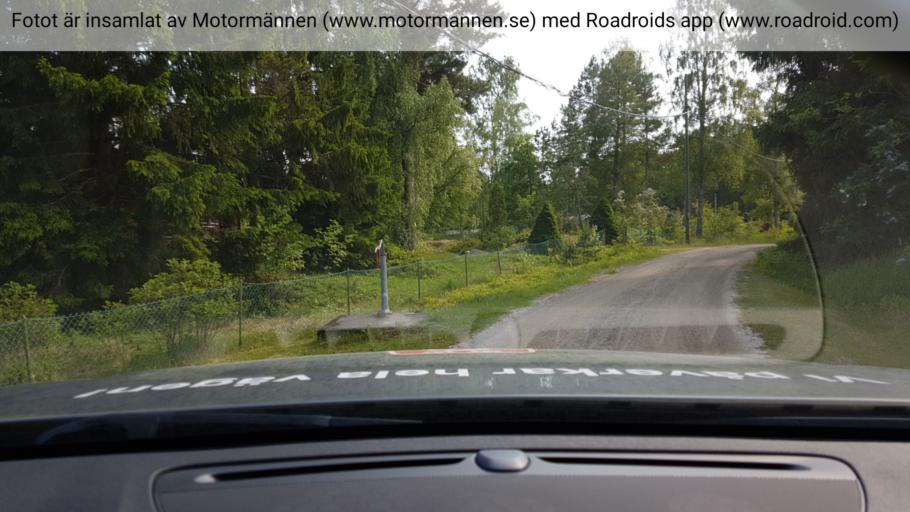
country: SE
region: Stockholm
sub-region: Varmdo Kommun
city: Mortnas
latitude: 59.2459
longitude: 18.4610
